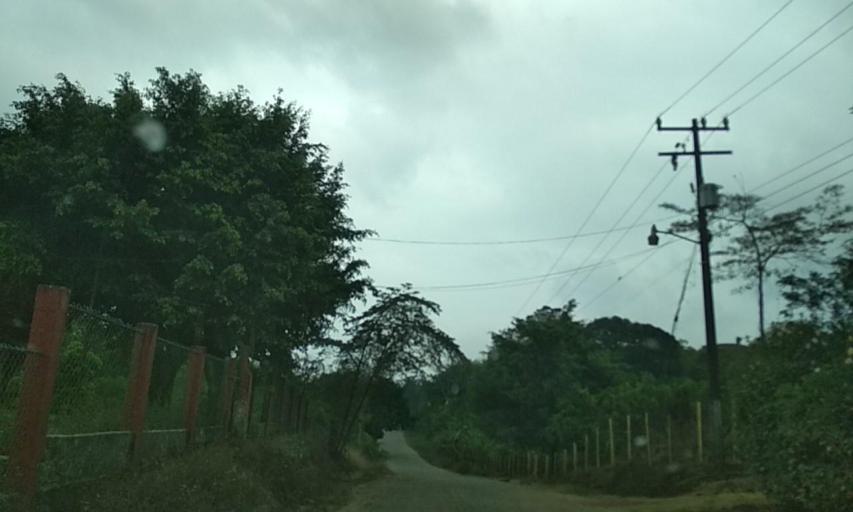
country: MX
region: Veracruz
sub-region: Uxpanapa
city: Poblado 10
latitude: 17.4590
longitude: -94.1033
